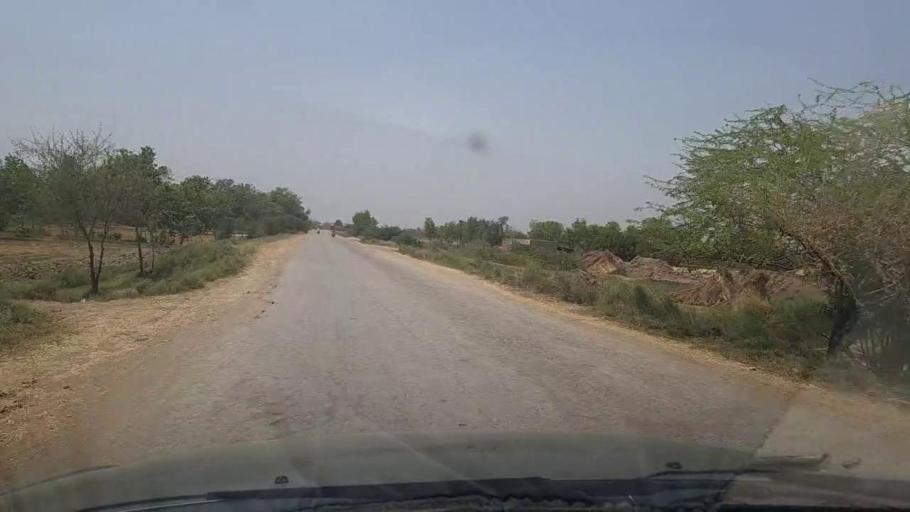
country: PK
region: Sindh
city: Karaundi
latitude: 26.8806
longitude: 68.3078
